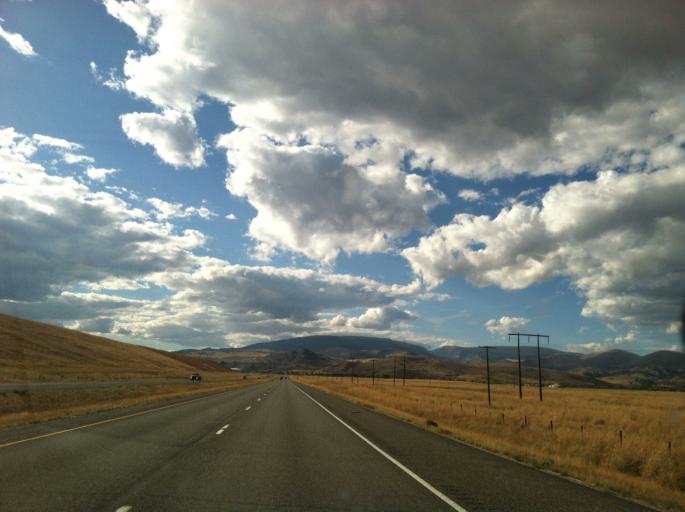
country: US
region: Montana
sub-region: Deer Lodge County
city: Anaconda
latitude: 46.1208
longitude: -112.8794
